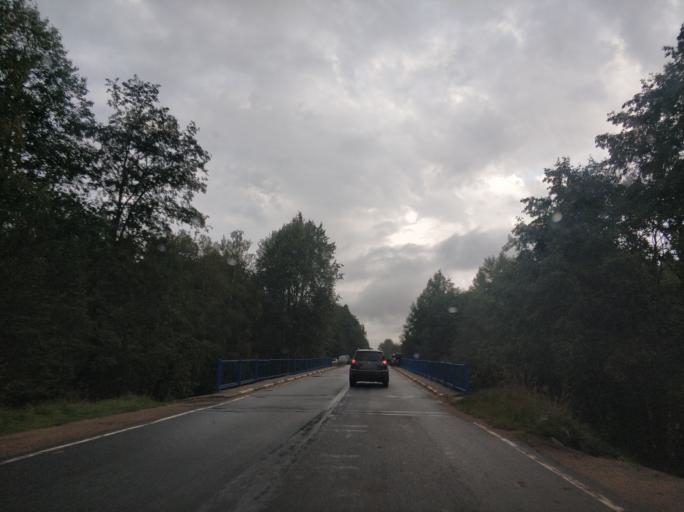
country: RU
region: Leningrad
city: Borisova Griva
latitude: 60.1348
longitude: 30.9601
